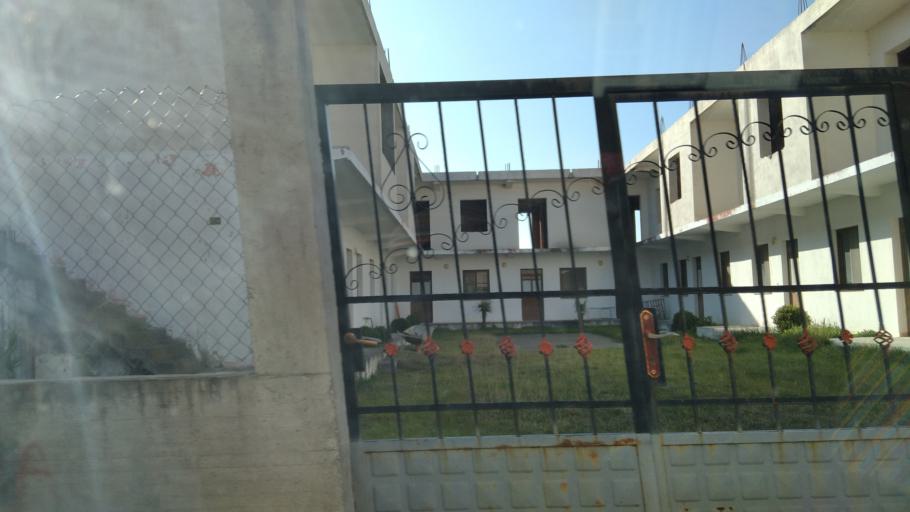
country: AL
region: Shkoder
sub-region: Rrethi i Shkodres
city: Velipoje
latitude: 41.8645
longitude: 19.4354
